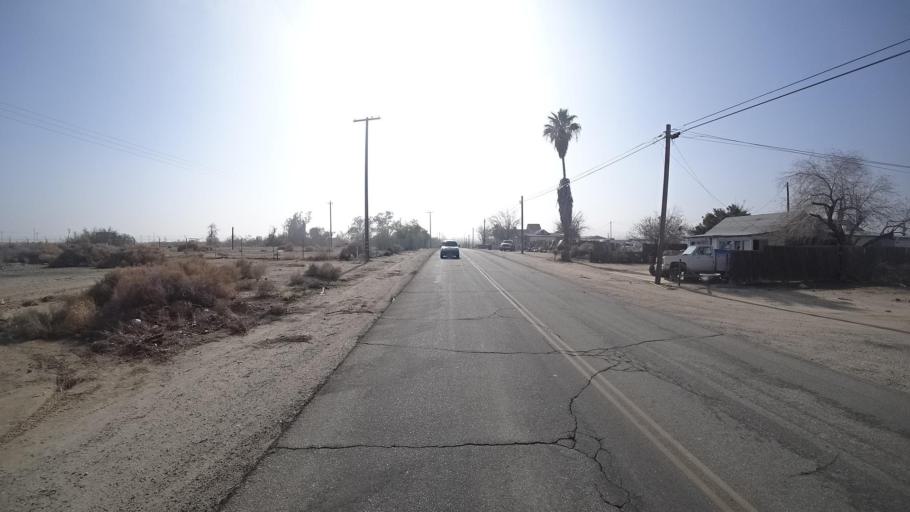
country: US
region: California
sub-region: Kern County
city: Ford City
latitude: 35.1696
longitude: -119.4652
